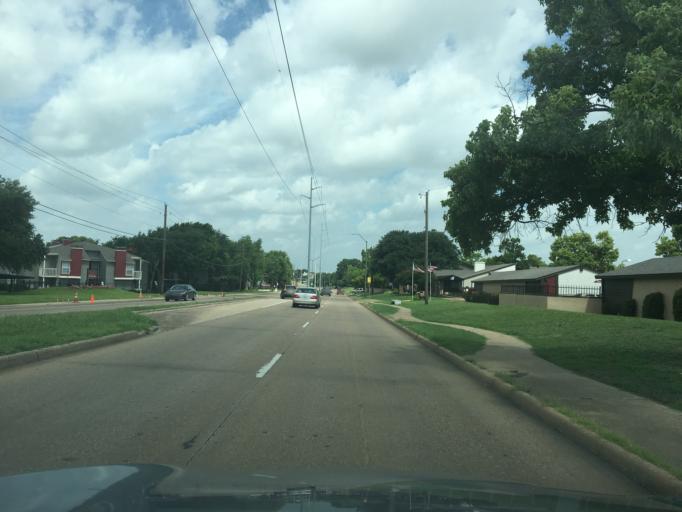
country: US
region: Texas
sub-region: Dallas County
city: Richardson
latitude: 32.9201
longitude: -96.7125
